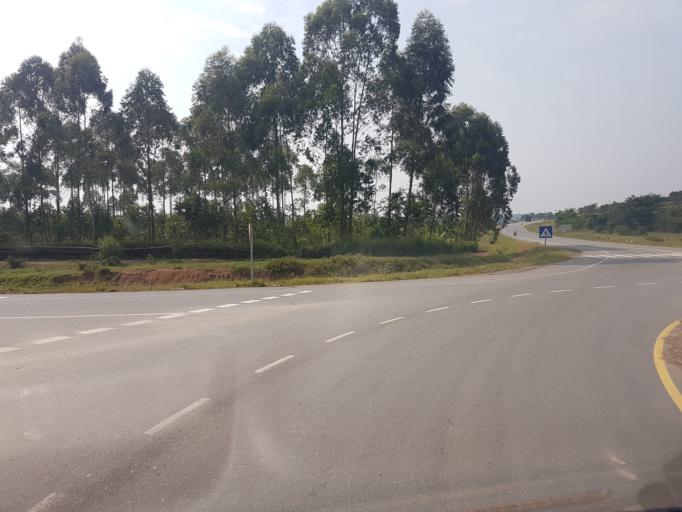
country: UG
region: Western Region
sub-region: Mbarara District
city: Bwizibwera
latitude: -0.6323
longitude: 30.5988
